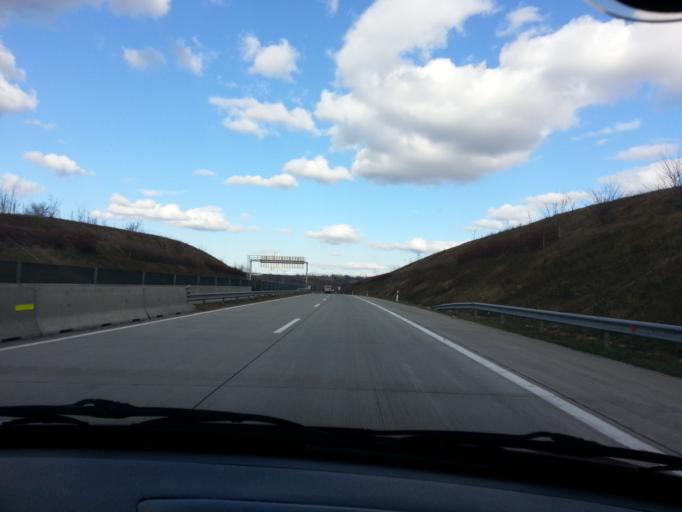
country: HU
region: Pest
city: Nagytarcsa
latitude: 47.5198
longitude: 19.3025
